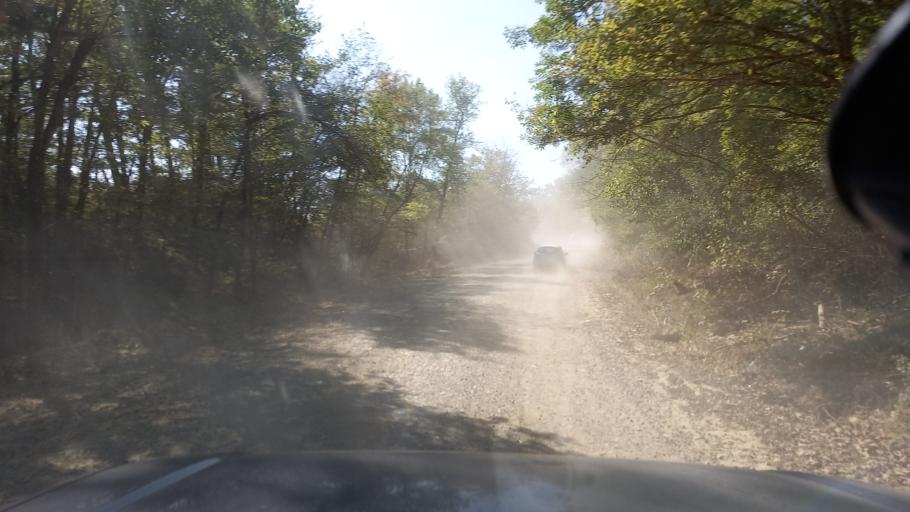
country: RU
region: Krasnodarskiy
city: Azovskaya
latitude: 44.6827
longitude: 38.6364
